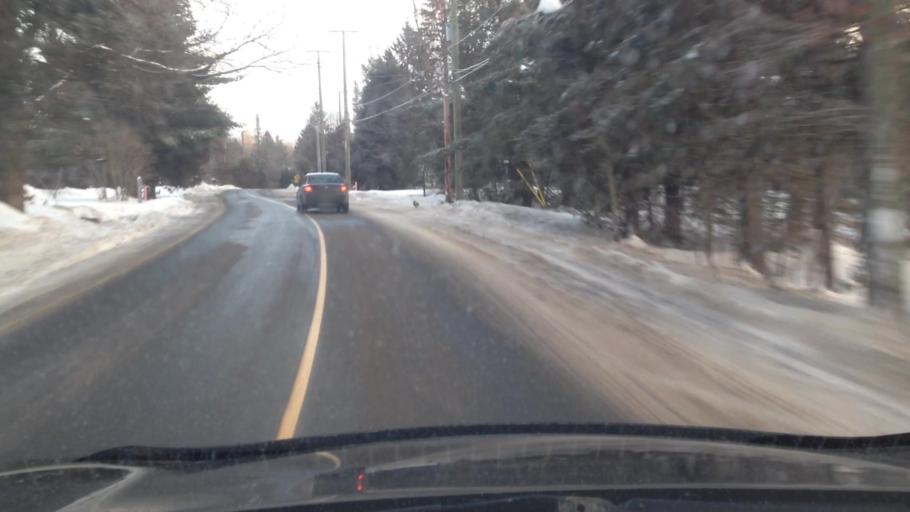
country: CA
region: Quebec
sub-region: Lanaudiere
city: Sainte-Julienne
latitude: 45.9522
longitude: -73.7520
